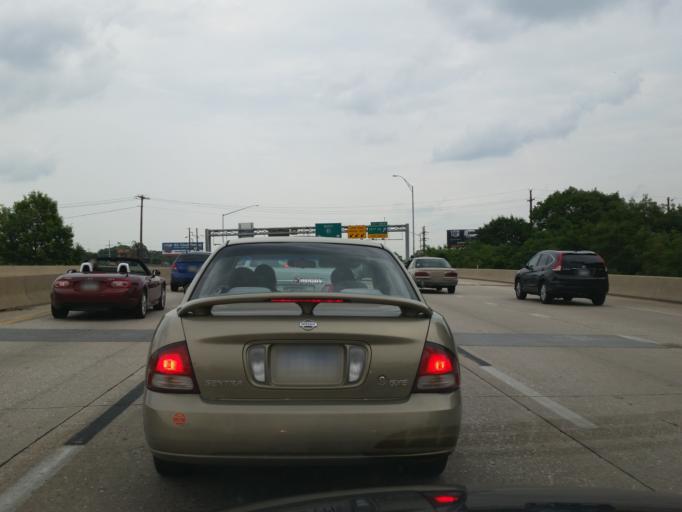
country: US
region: Pennsylvania
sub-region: Dauphin County
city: Penbrook
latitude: 40.2559
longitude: -76.8606
